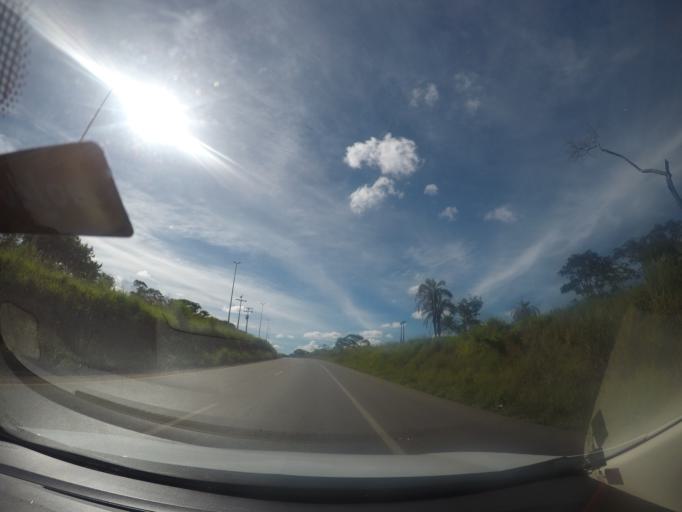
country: BR
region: Goias
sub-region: Inhumas
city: Inhumas
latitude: -16.4071
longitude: -49.4780
